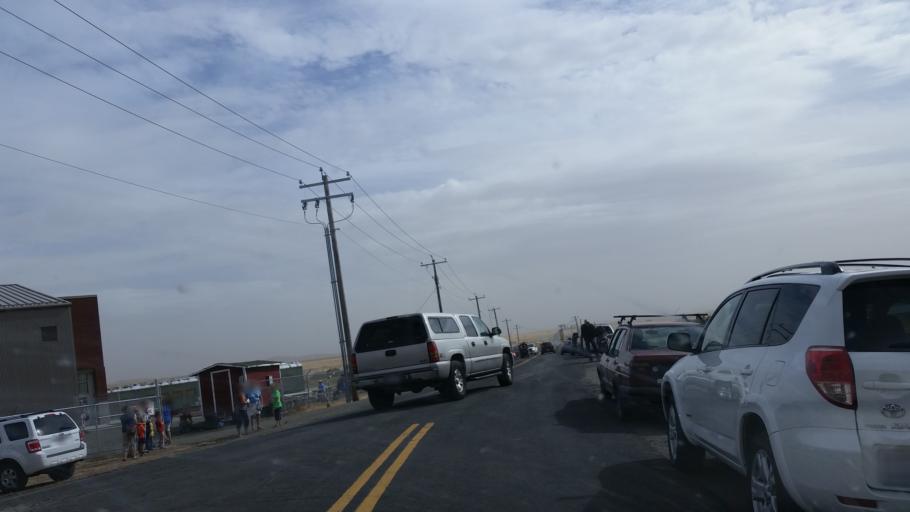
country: US
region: Washington
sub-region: Lincoln County
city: Davenport
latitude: 47.6641
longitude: -117.9381
